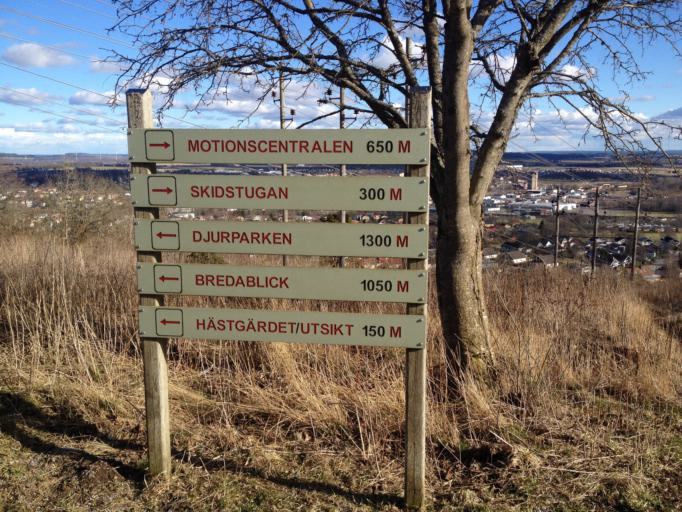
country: SE
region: Vaestra Goetaland
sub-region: Falkopings Kommun
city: Falkoeping
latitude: 58.1757
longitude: 13.5289
